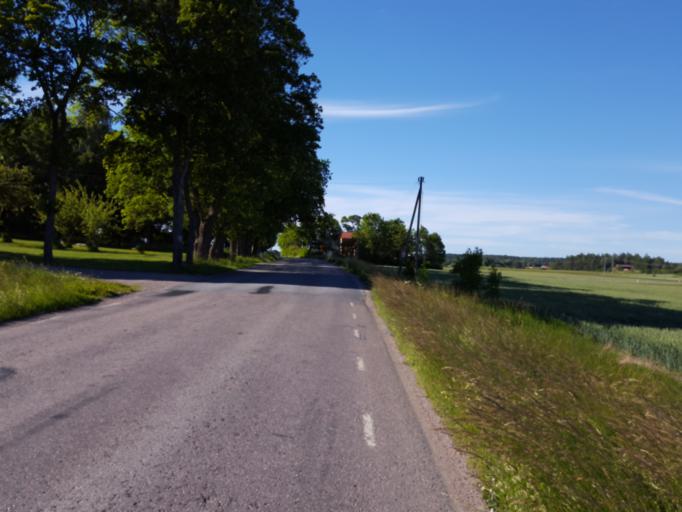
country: SE
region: Uppsala
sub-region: Uppsala Kommun
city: Saevja
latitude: 59.8419
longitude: 17.7417
